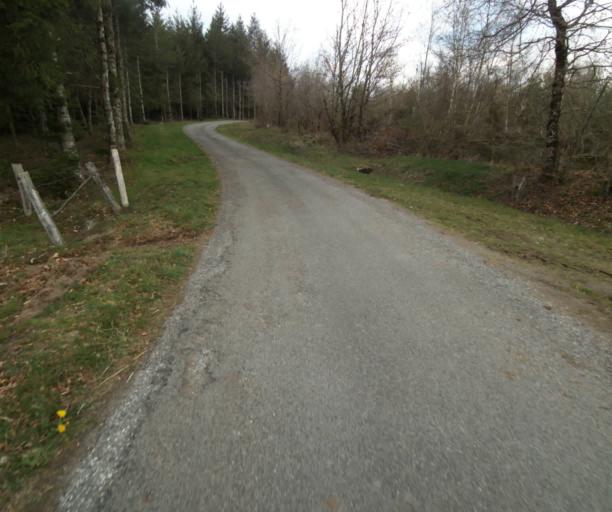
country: FR
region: Limousin
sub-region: Departement de la Correze
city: Correze
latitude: 45.2698
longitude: 1.9549
